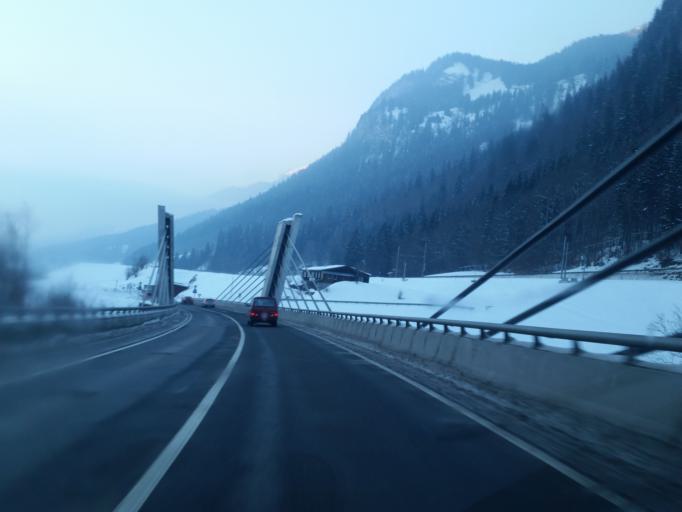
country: CH
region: Grisons
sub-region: Praettigau/Davos District
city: Klosters Serneus
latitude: 46.8859
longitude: 9.8565
